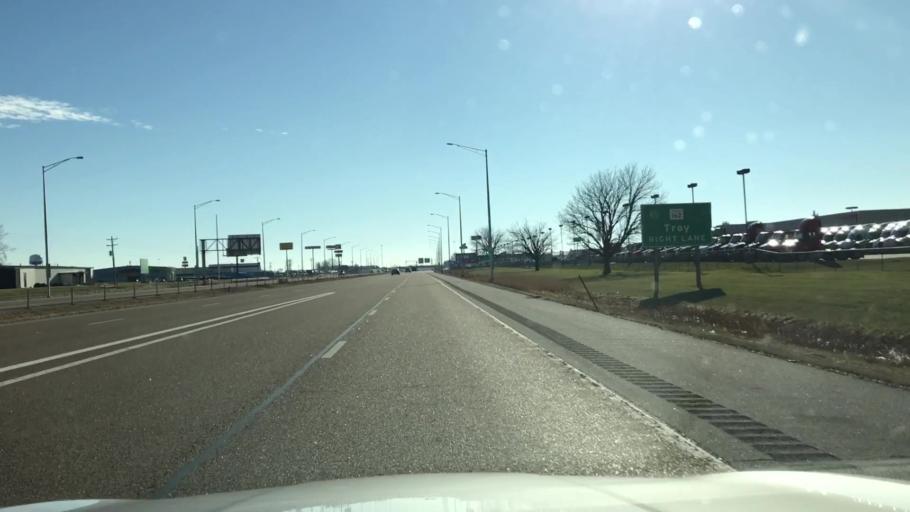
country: US
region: Illinois
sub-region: Madison County
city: Troy
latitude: 38.7421
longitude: -89.9101
